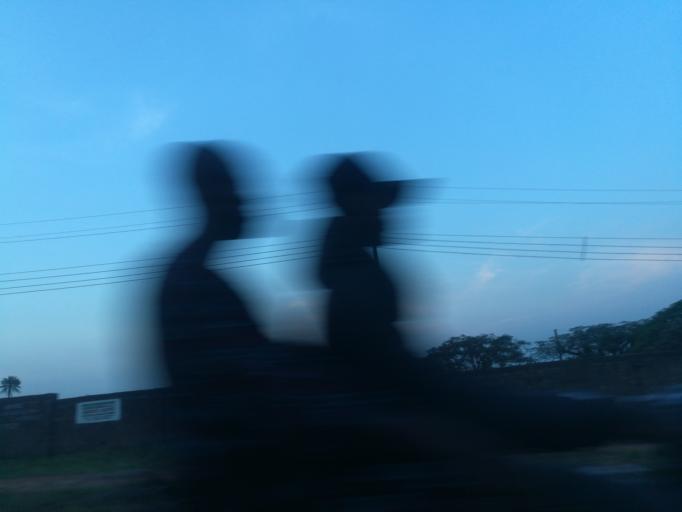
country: NG
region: Ogun
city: Abeokuta
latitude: 7.1790
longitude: 3.4040
